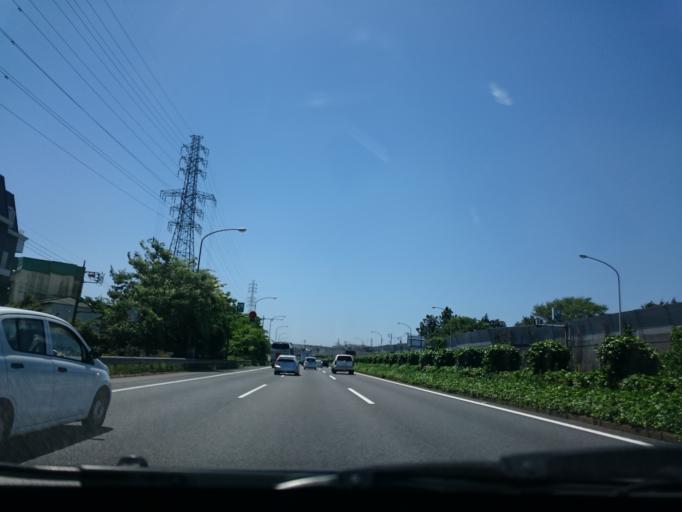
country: JP
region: Kanagawa
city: Minami-rinkan
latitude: 35.5032
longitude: 139.4797
